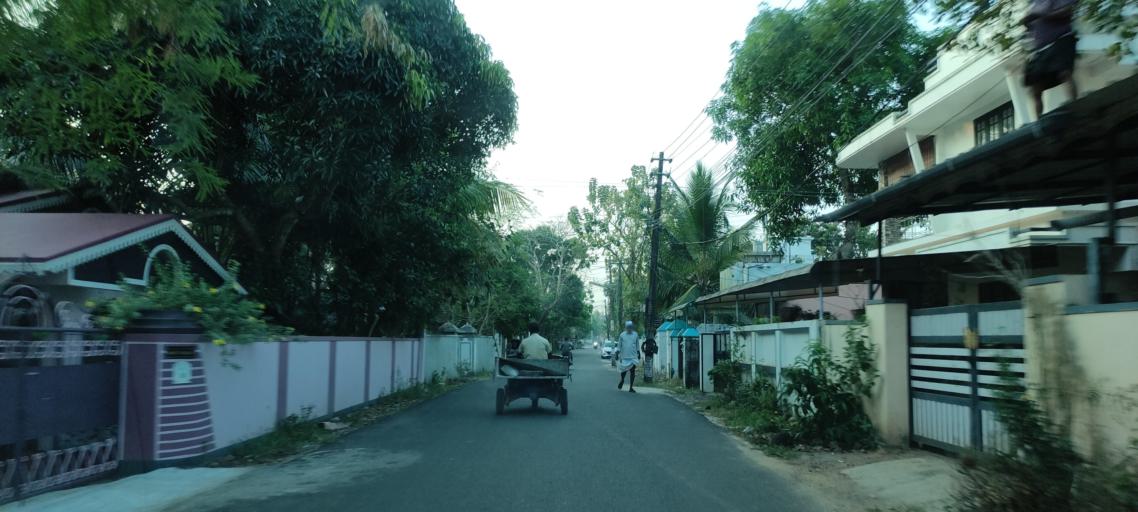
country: IN
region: Kerala
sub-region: Alappuzha
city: Alleppey
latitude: 9.4251
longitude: 76.3483
